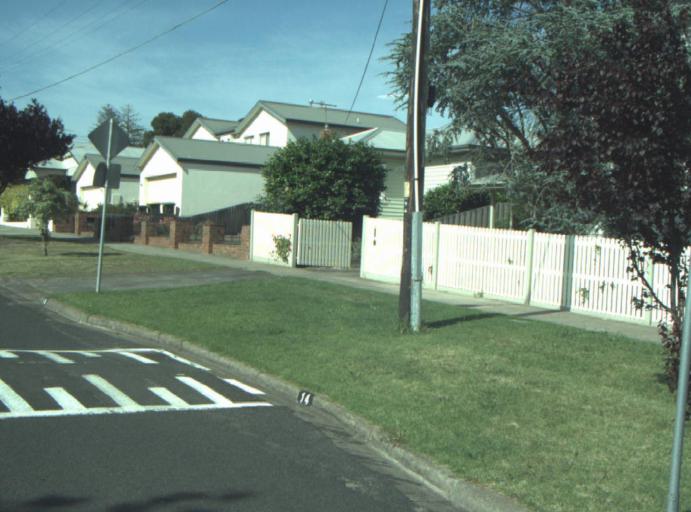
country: AU
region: Victoria
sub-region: Greater Geelong
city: Hamlyn Heights
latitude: -38.1280
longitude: 144.3318
